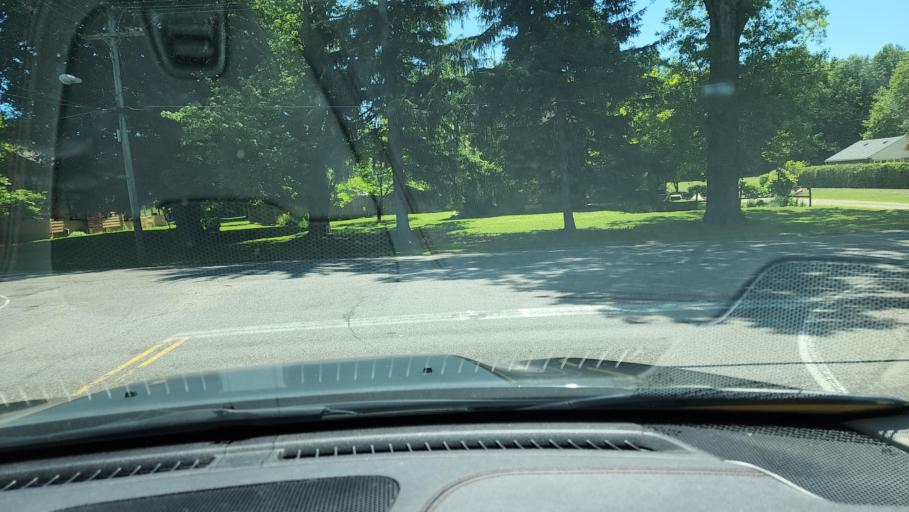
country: US
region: Ohio
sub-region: Trumbull County
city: Niles
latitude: 41.1684
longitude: -80.7825
